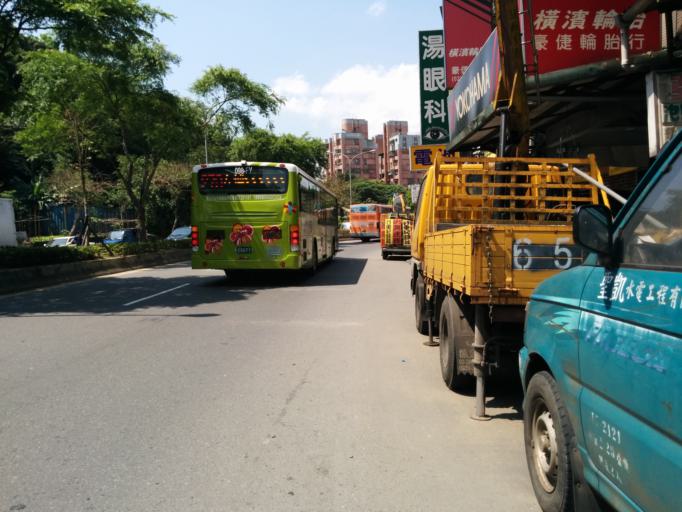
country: TW
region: Taipei
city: Taipei
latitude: 25.0499
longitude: 121.6158
